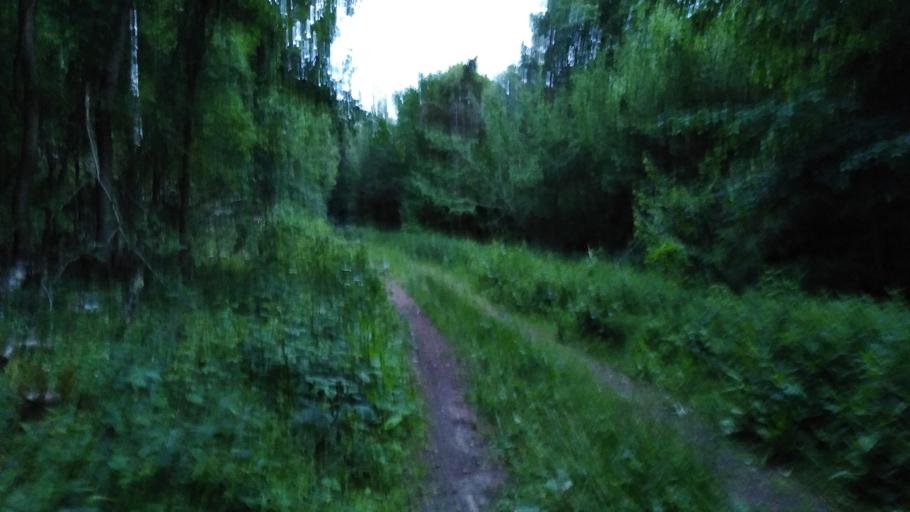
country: DE
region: Schleswig-Holstein
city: Kabelhorst
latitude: 54.2299
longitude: 10.9138
